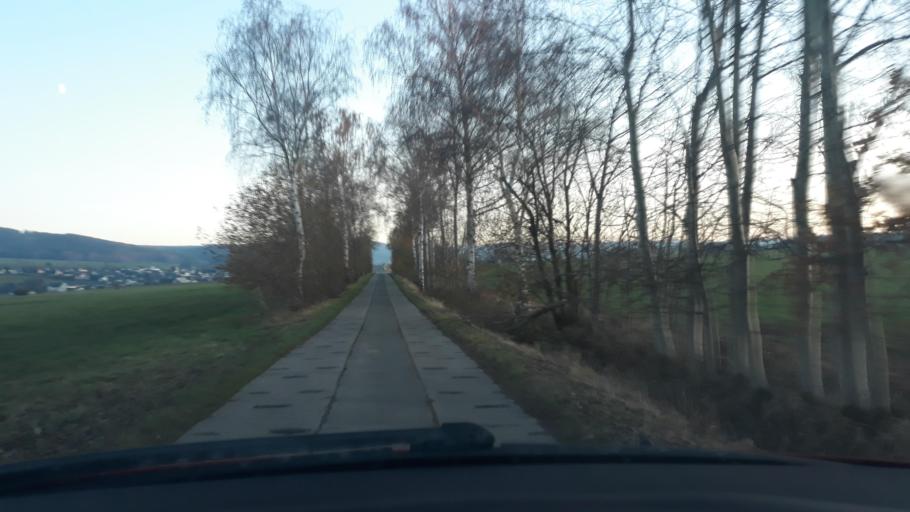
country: DE
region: Saxony
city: Kirchberg
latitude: 50.6062
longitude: 12.5376
